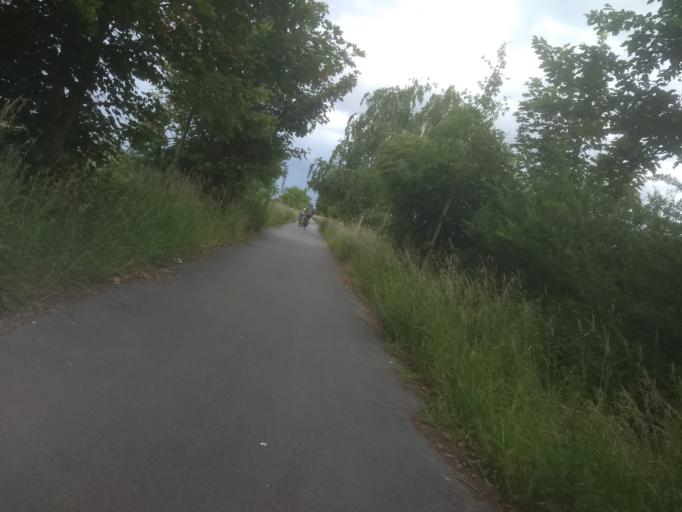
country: FR
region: Nord-Pas-de-Calais
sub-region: Departement du Pas-de-Calais
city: Riviere
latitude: 50.2533
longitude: 2.6980
